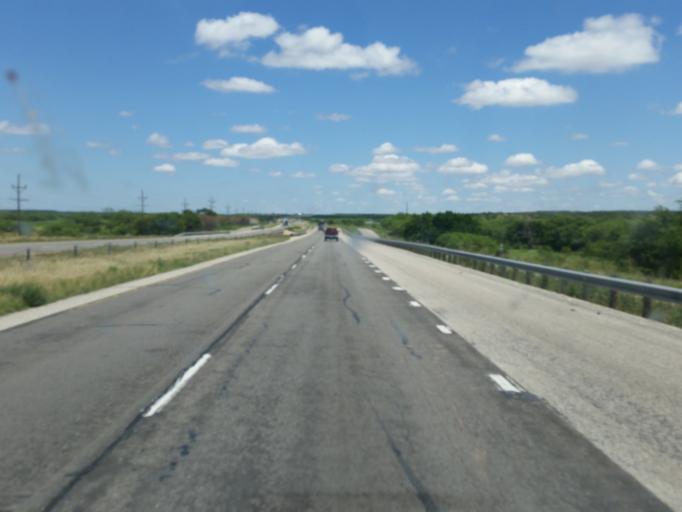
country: US
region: Texas
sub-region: Nolan County
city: Sweetwater
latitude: 32.4943
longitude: -100.2951
